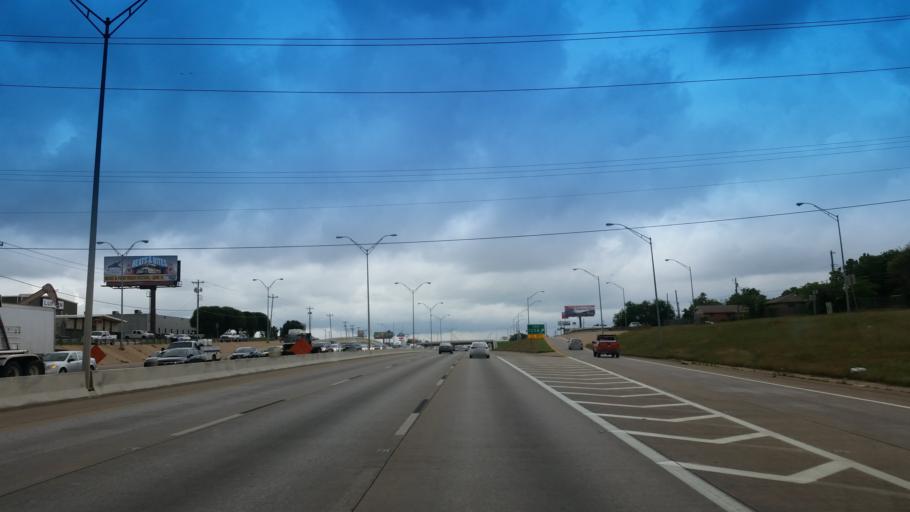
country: US
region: Oklahoma
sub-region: Oklahoma County
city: Oklahoma City
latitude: 35.4432
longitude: -97.4863
